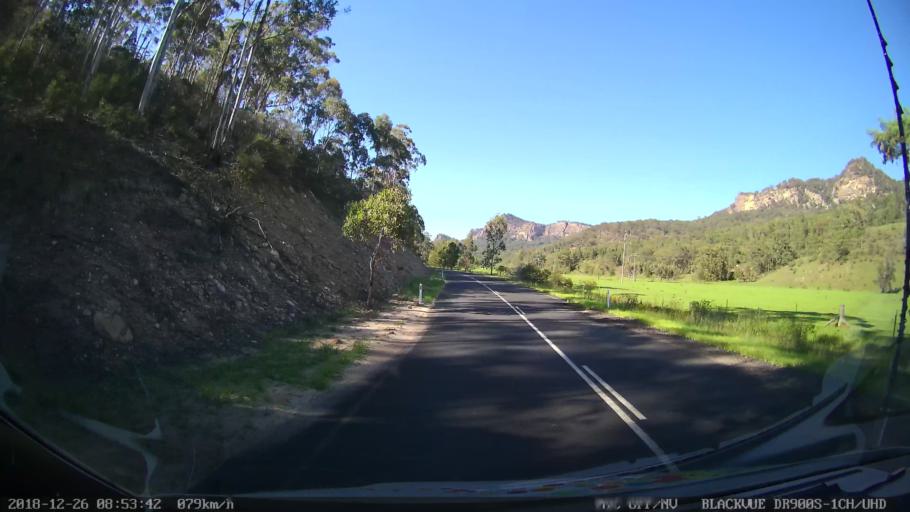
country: AU
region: New South Wales
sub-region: Mid-Western Regional
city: Kandos
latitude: -32.6072
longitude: 150.0762
